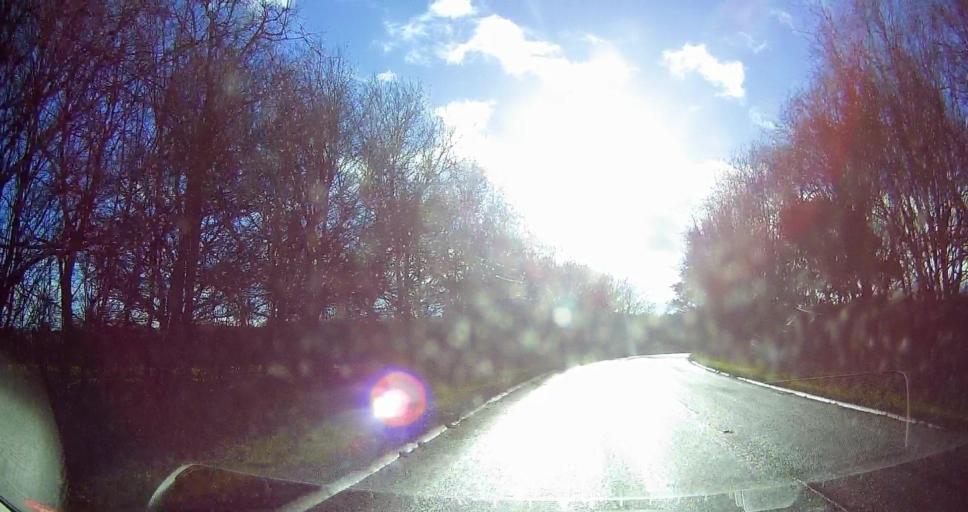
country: GB
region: England
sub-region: Kent
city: Westerham
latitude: 51.2755
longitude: 0.0846
